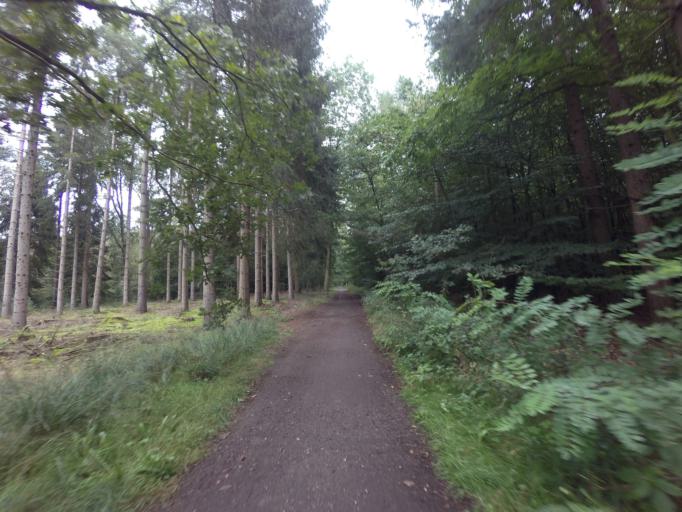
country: DE
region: North Rhine-Westphalia
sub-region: Regierungsbezirk Munster
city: Gronau
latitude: 52.2397
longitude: 7.0913
